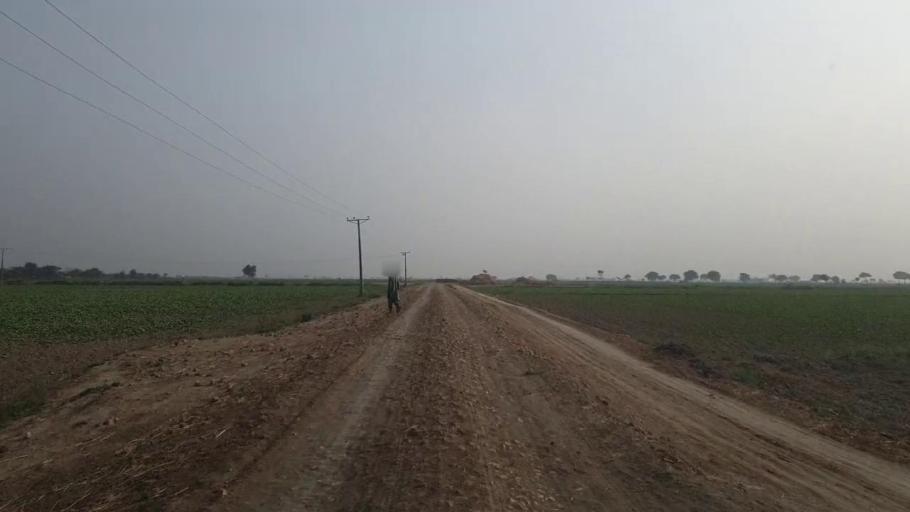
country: PK
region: Sindh
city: Mirpur Batoro
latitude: 24.5605
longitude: 68.4186
